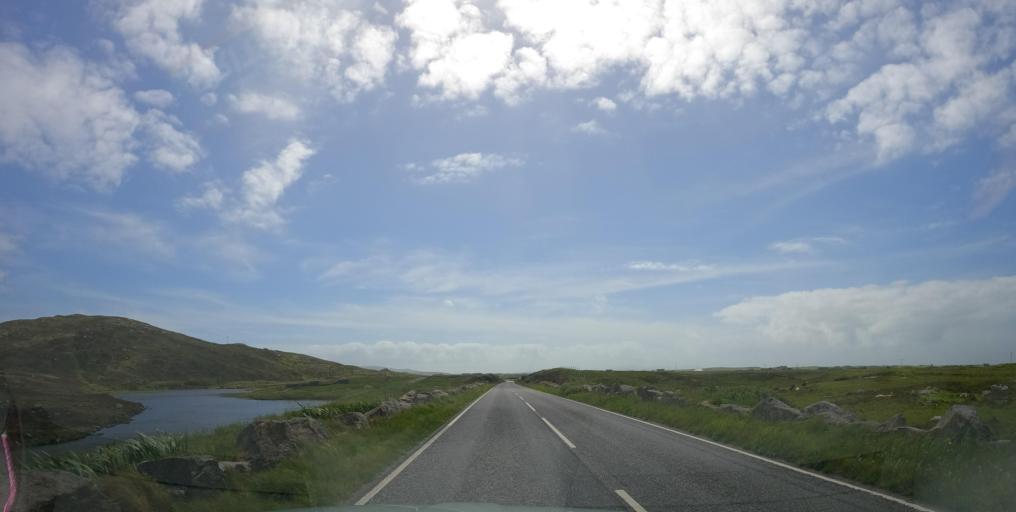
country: GB
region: Scotland
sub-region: Eilean Siar
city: Isle of South Uist
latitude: 57.1938
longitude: -7.3891
